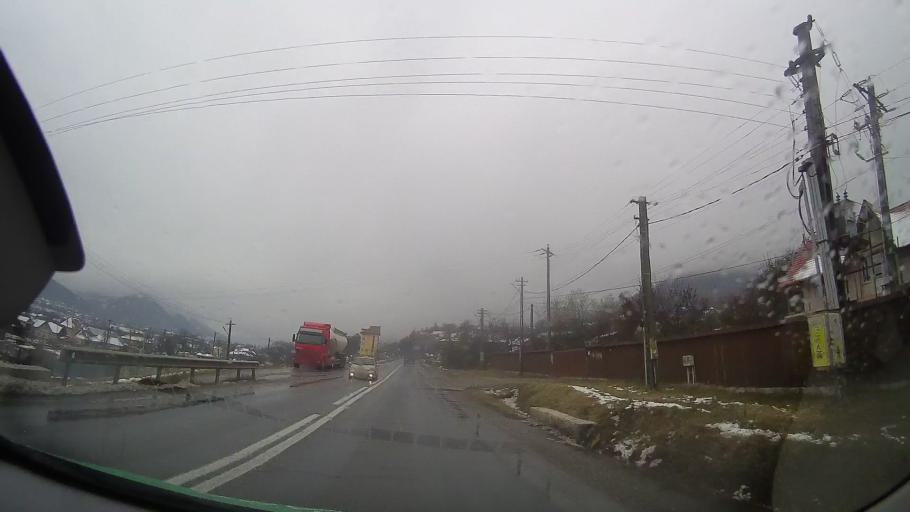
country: RO
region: Neamt
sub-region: Comuna Alexandru Cel Bun
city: Bistrita
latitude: 46.9414
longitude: 26.2767
